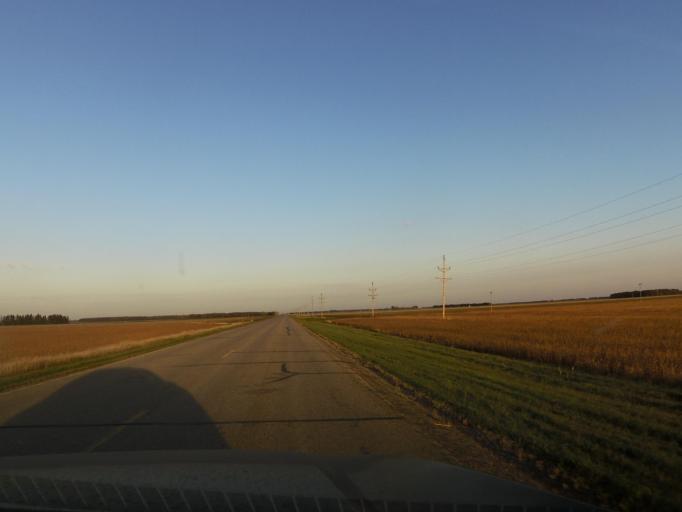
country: CA
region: Manitoba
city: Altona
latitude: 48.9636
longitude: -97.5710
